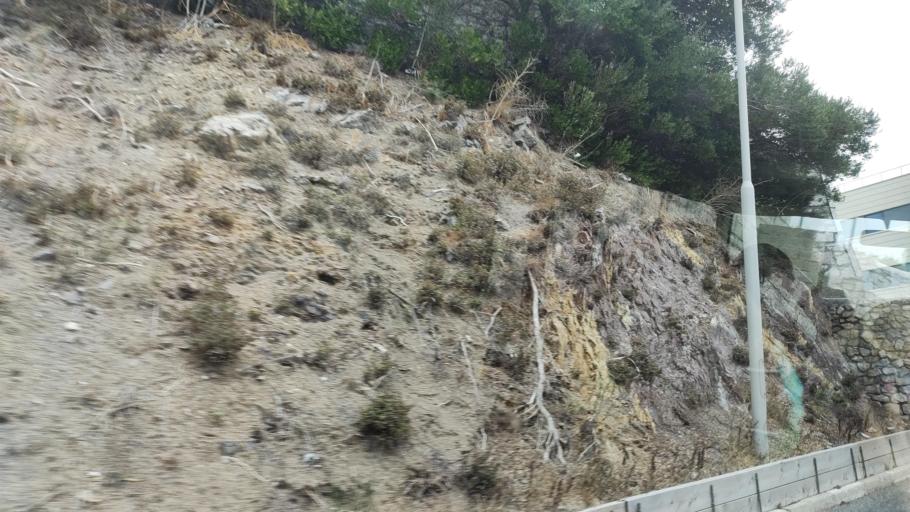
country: GI
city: Gibraltar
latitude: 36.1189
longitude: -5.3457
